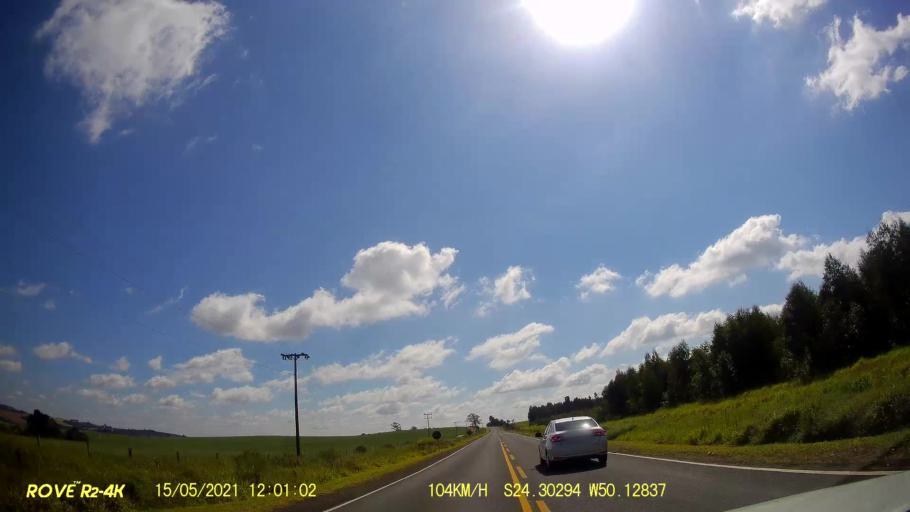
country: BR
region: Parana
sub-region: Pirai Do Sul
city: Pirai do Sul
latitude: -24.3027
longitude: -50.1281
